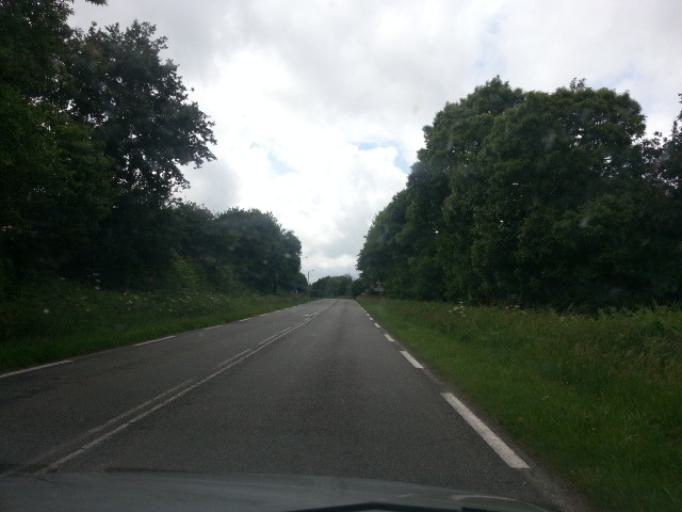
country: FR
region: Brittany
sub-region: Departement du Finistere
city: Rosporden
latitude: 47.9544
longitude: -3.8094
